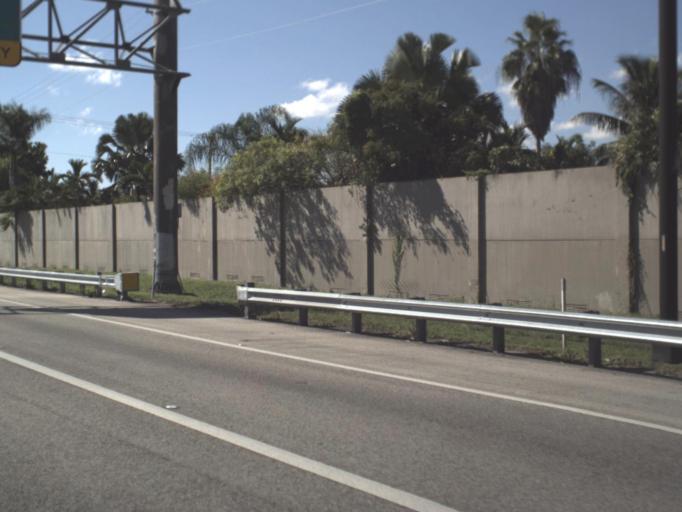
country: US
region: Florida
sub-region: Miami-Dade County
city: Westwood Lake
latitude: 25.7380
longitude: -80.3846
